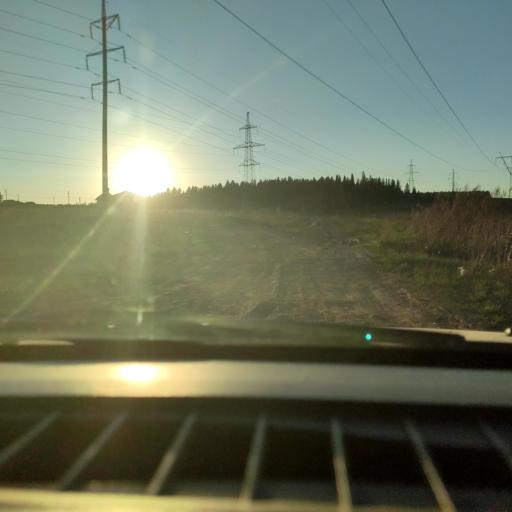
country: RU
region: Perm
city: Ferma
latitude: 57.9517
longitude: 56.3632
